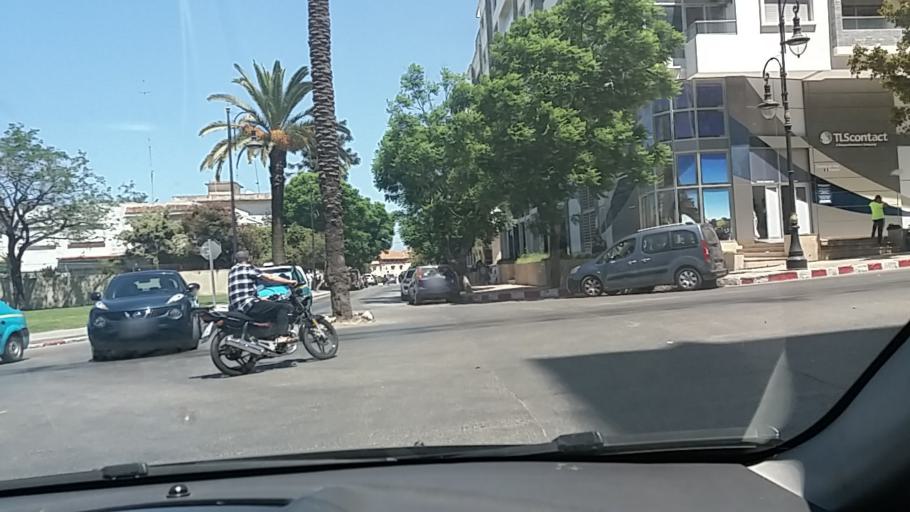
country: MA
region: Tanger-Tetouan
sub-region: Tanger-Assilah
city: Tangier
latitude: 35.7835
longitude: -5.8219
